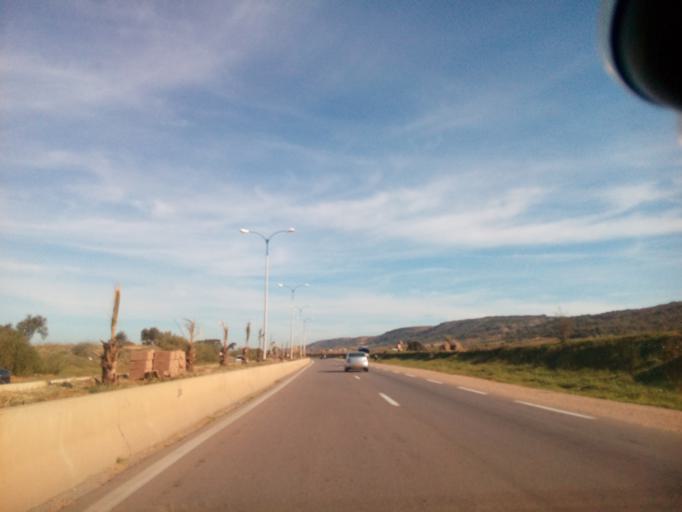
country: DZ
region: Mostaganem
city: Mostaganem
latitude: 35.8476
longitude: 0.0189
